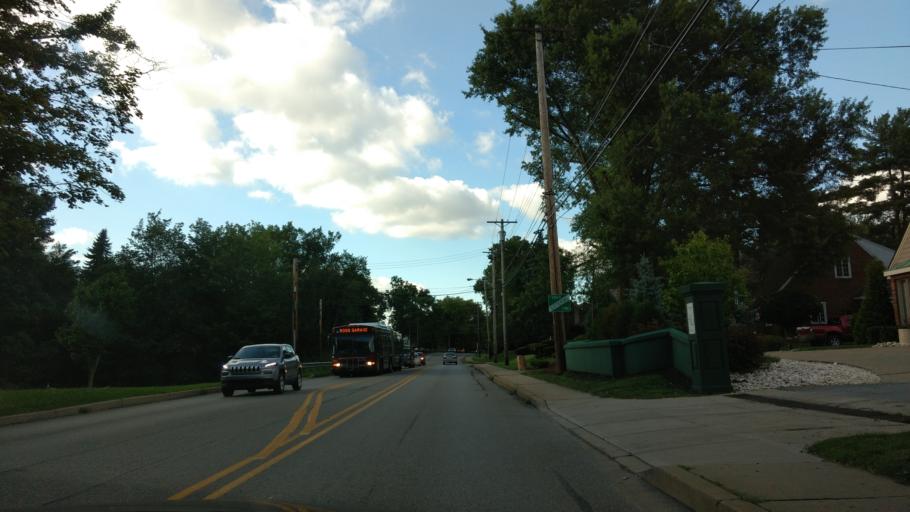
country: US
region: Pennsylvania
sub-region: Allegheny County
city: West View
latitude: 40.5262
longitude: -80.0356
